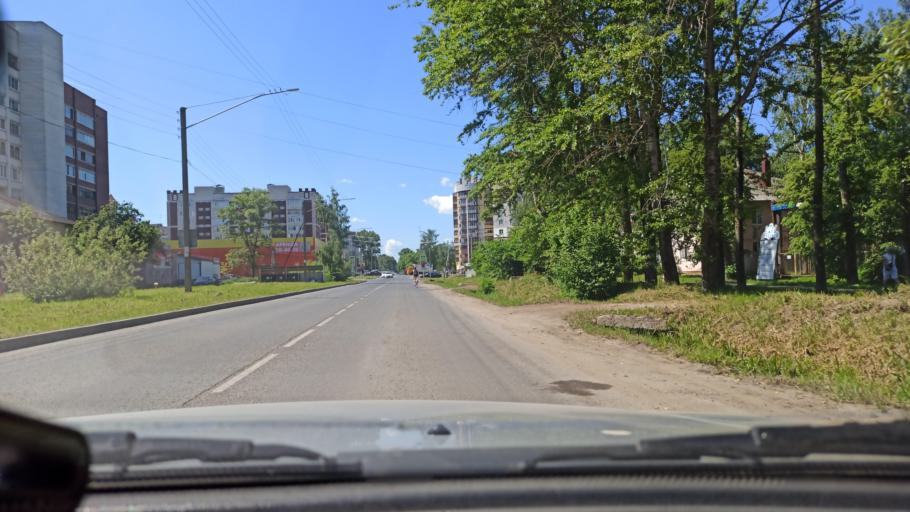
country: RU
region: Vologda
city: Vologda
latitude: 59.2181
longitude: 39.8517
